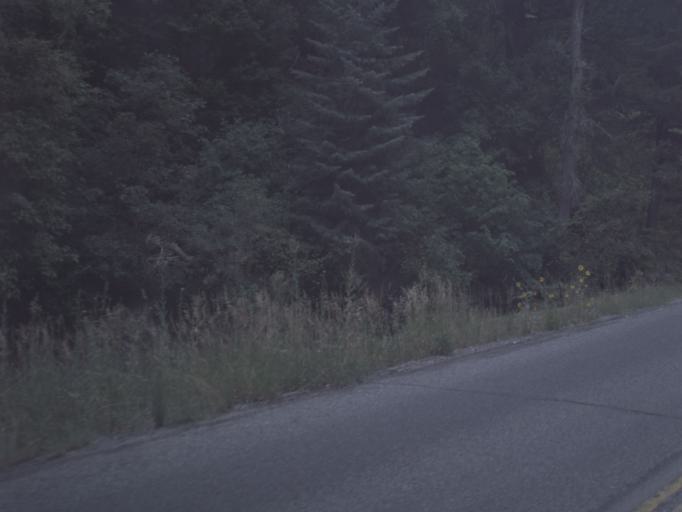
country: US
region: Utah
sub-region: Utah County
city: Orem
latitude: 40.3734
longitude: -111.5689
